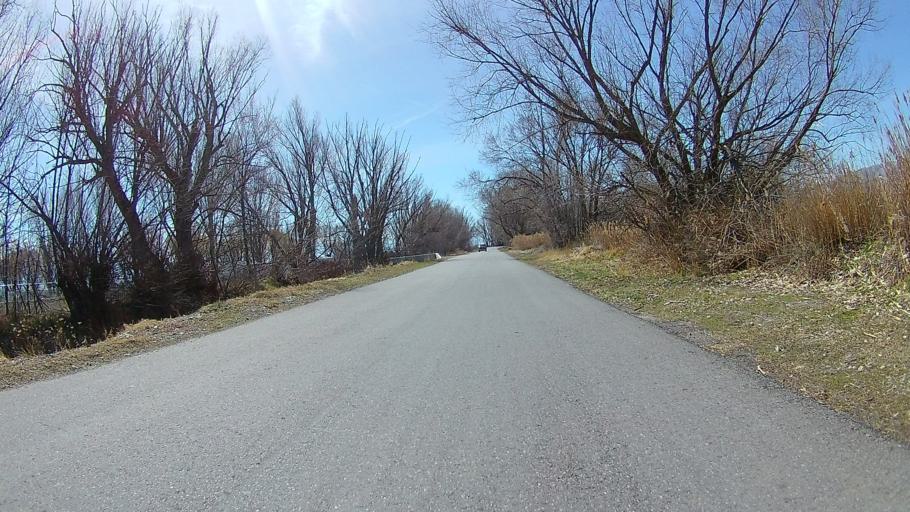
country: US
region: Utah
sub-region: Utah County
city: American Fork
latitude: 40.3464
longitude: -111.8017
